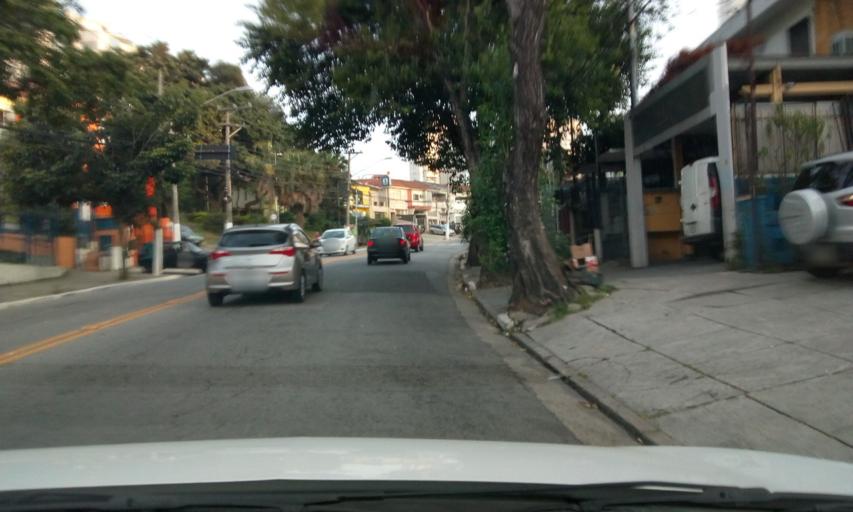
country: BR
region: Sao Paulo
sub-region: Sao Paulo
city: Sao Paulo
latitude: -23.5427
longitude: -46.6902
